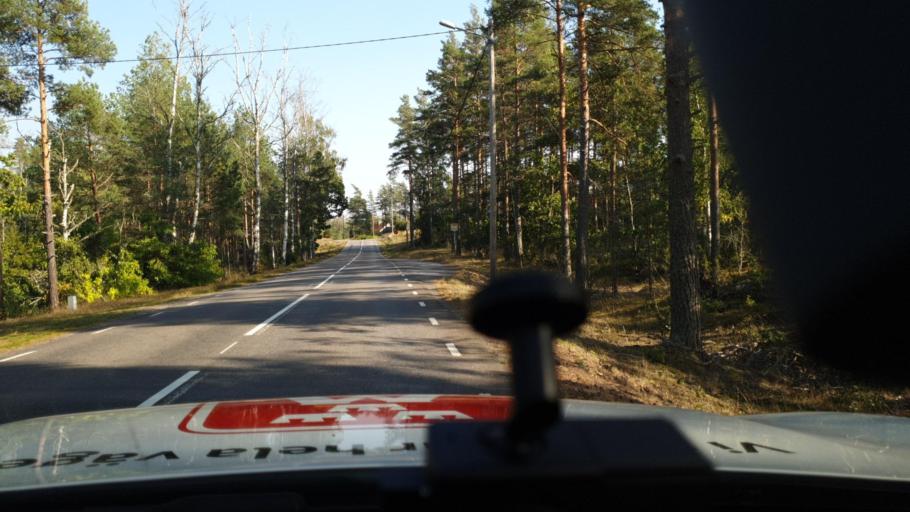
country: SE
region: Kalmar
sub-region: Oskarshamns Kommun
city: Oskarshamn
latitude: 57.4411
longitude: 16.4072
